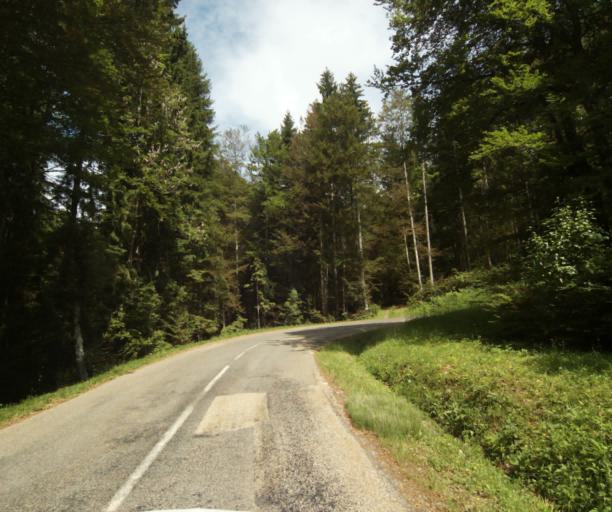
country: FR
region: Rhone-Alpes
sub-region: Departement de la Haute-Savoie
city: Perrignier
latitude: 46.2841
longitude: 6.4728
